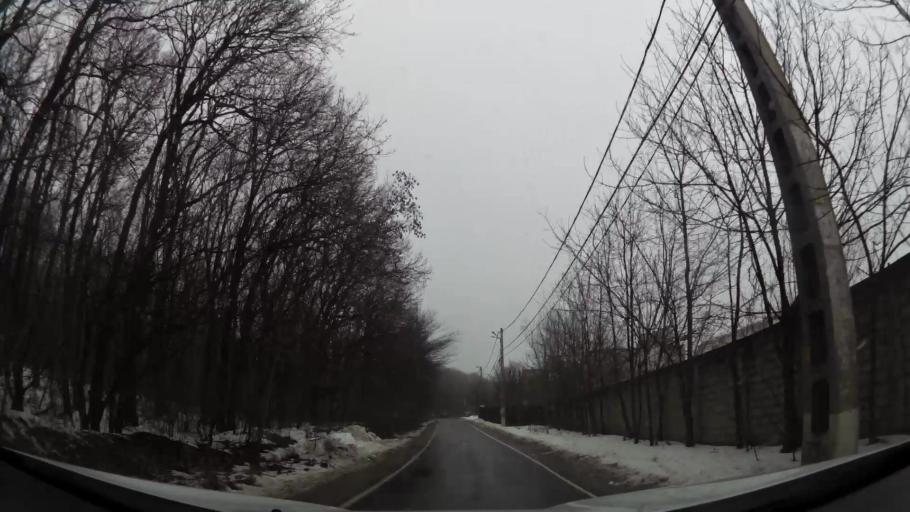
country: RO
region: Ilfov
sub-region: Comuna Chiajna
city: Rosu
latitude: 44.4530
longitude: 26.0007
